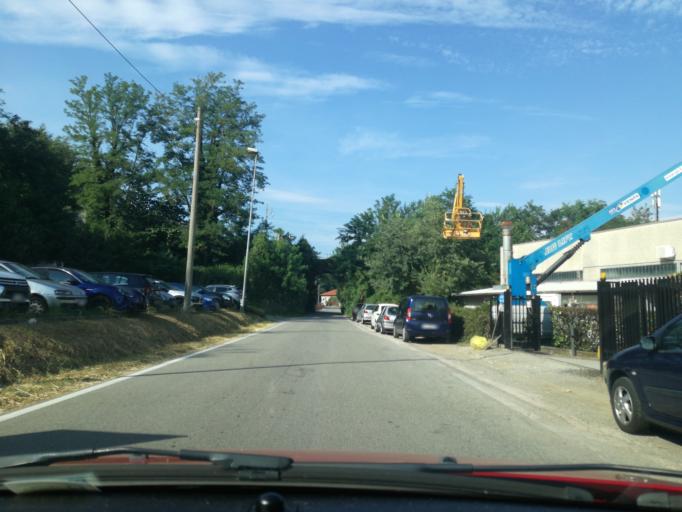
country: IT
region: Lombardy
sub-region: Provincia di Monza e Brianza
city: Camparada
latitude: 45.6448
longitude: 9.3393
